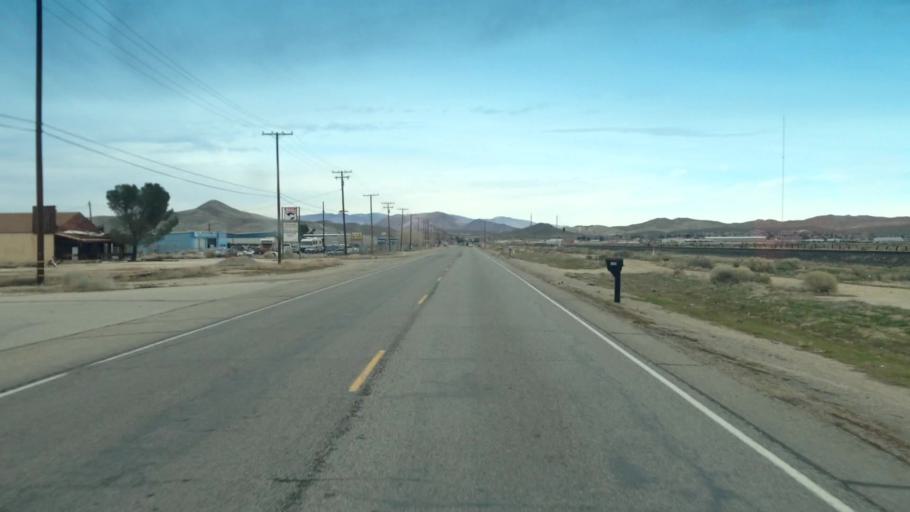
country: US
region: California
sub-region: Kern County
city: Rosamond
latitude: 34.8406
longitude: -118.1592
